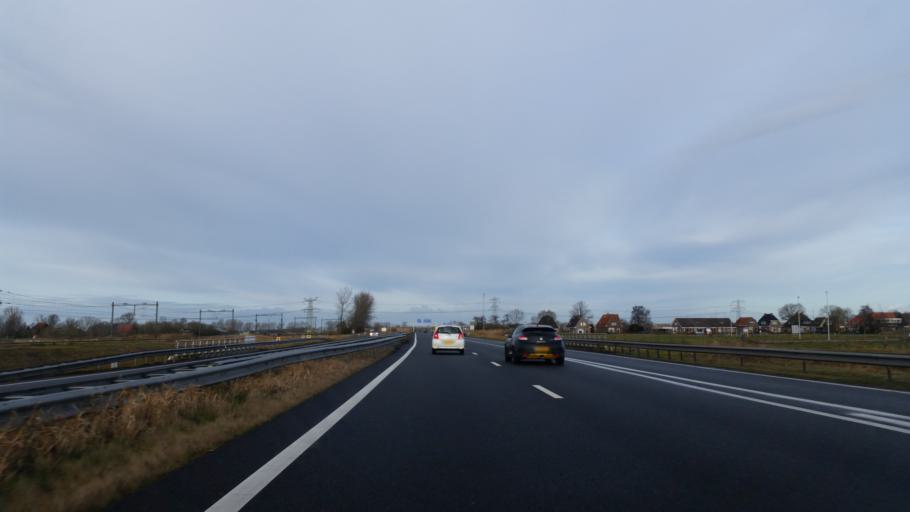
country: NL
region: Friesland
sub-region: Gemeente Leeuwarden
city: Wirdum
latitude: 53.1444
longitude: 5.7965
